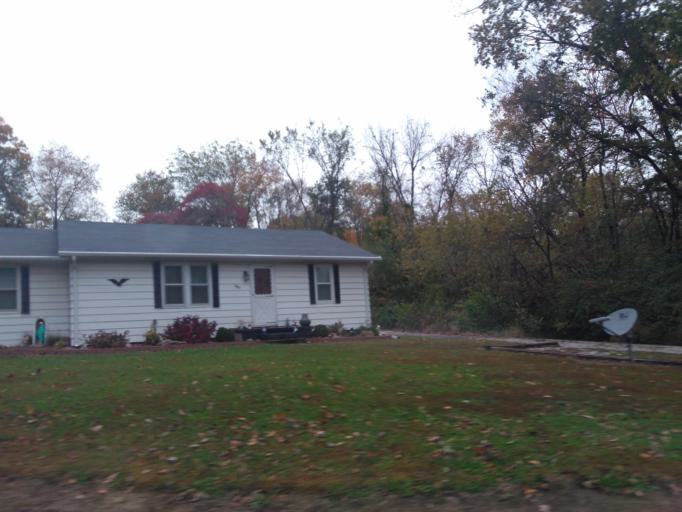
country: US
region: Illinois
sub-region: Bond County
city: Greenville
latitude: 38.9005
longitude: -89.4019
